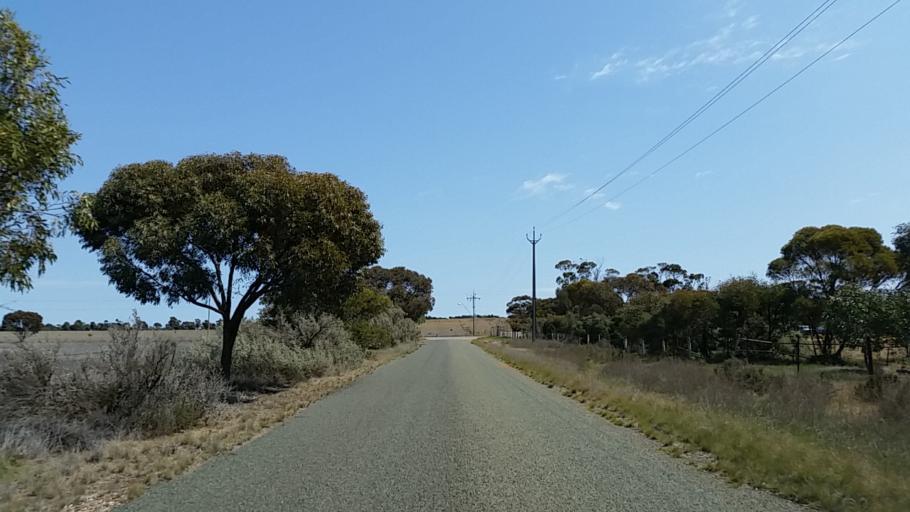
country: AU
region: South Australia
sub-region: Peterborough
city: Peterborough
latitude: -32.9595
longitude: 138.8483
